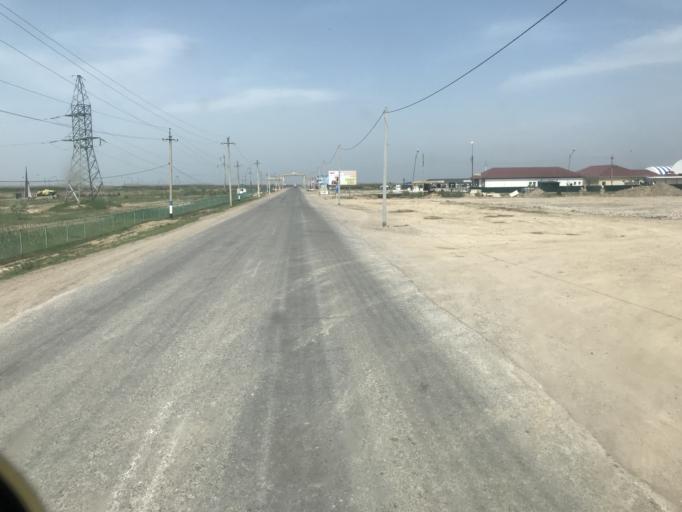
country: KZ
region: Ongtustik Qazaqstan
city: Asykata
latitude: 40.9604
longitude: 68.4616
